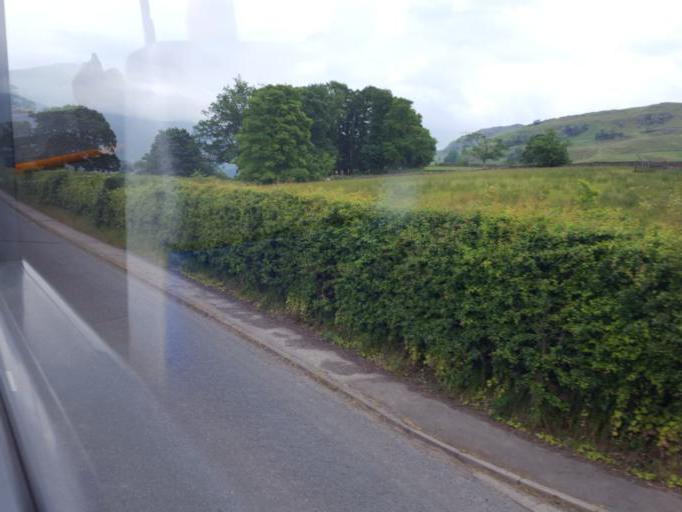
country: GB
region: England
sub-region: Cumbria
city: Keswick
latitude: 54.5962
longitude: -3.1071
